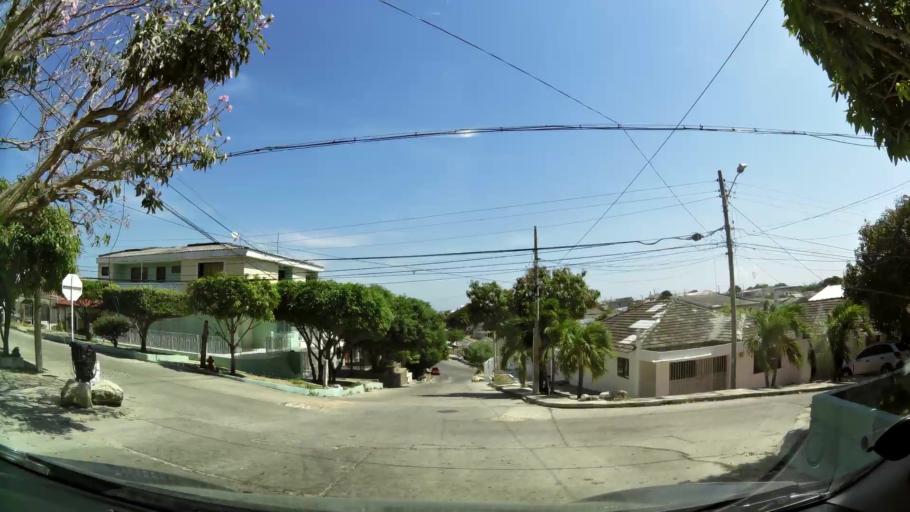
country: CO
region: Atlantico
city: Barranquilla
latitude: 10.9798
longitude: -74.7971
